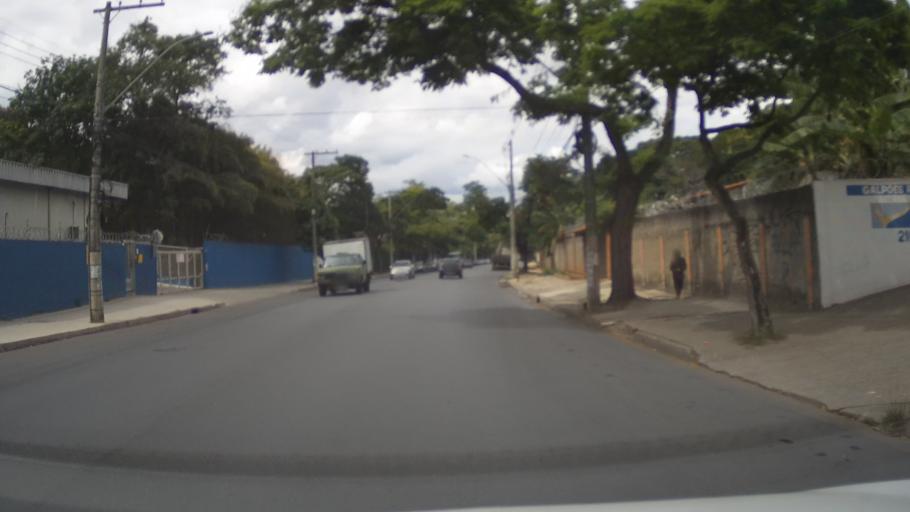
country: BR
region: Minas Gerais
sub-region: Belo Horizonte
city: Belo Horizonte
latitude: -19.8231
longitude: -43.9561
